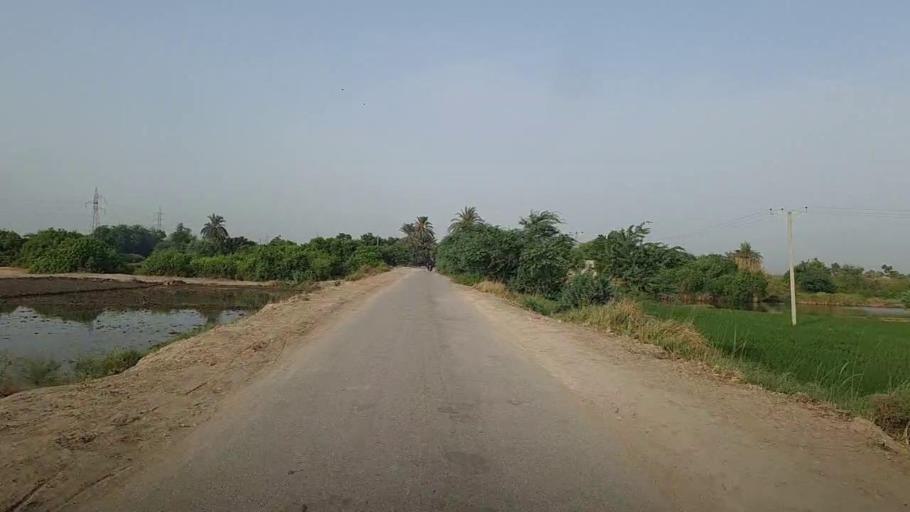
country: PK
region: Sindh
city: Mehar
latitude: 27.1492
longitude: 67.7996
